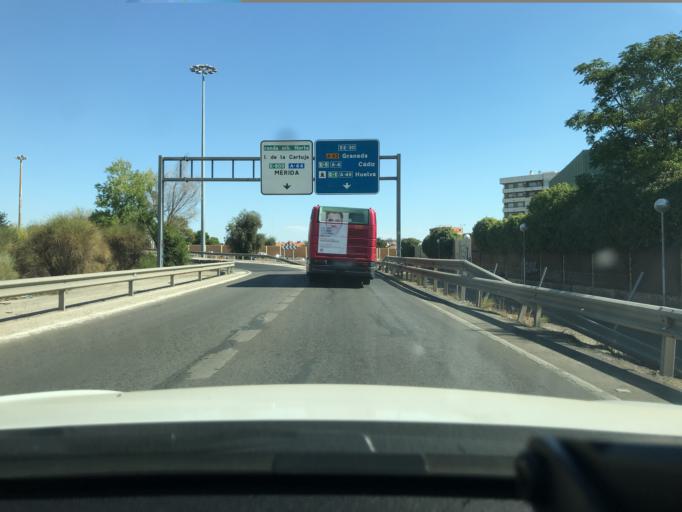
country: ES
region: Andalusia
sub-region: Provincia de Sevilla
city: Sevilla
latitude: 37.4072
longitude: -5.9504
